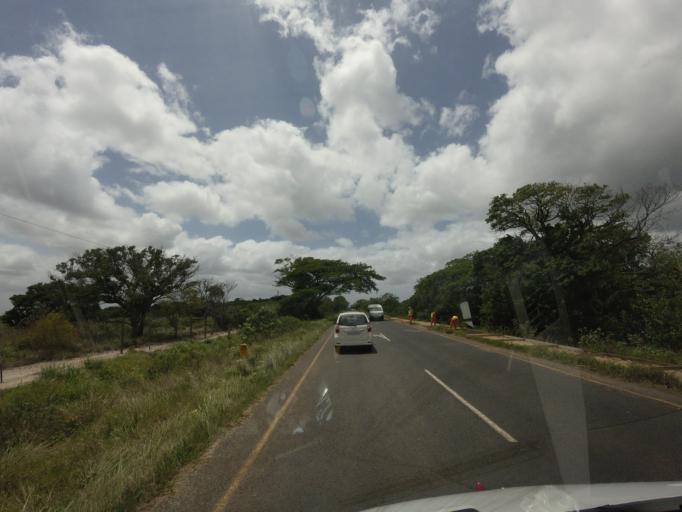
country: ZA
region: KwaZulu-Natal
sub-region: uMkhanyakude District Municipality
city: Mtubatuba
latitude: -28.3750
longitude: 32.3847
